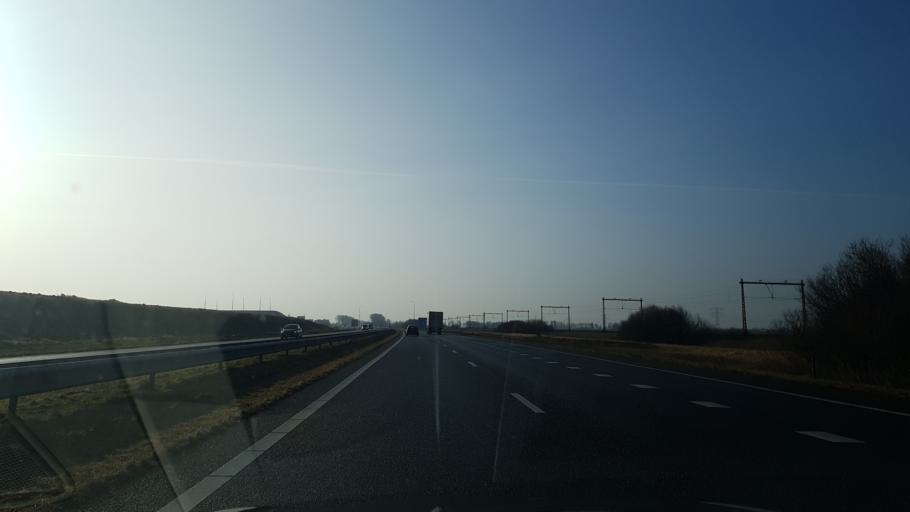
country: NL
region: Friesland
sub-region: Gemeente Boarnsterhim
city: Grou
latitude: 53.1047
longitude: 5.8159
